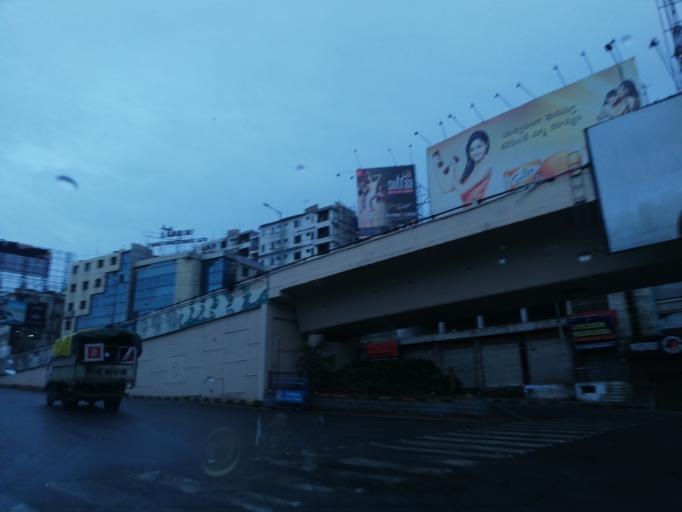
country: IN
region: Telangana
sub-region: Hyderabad
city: Hyderabad
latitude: 17.4258
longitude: 78.4487
